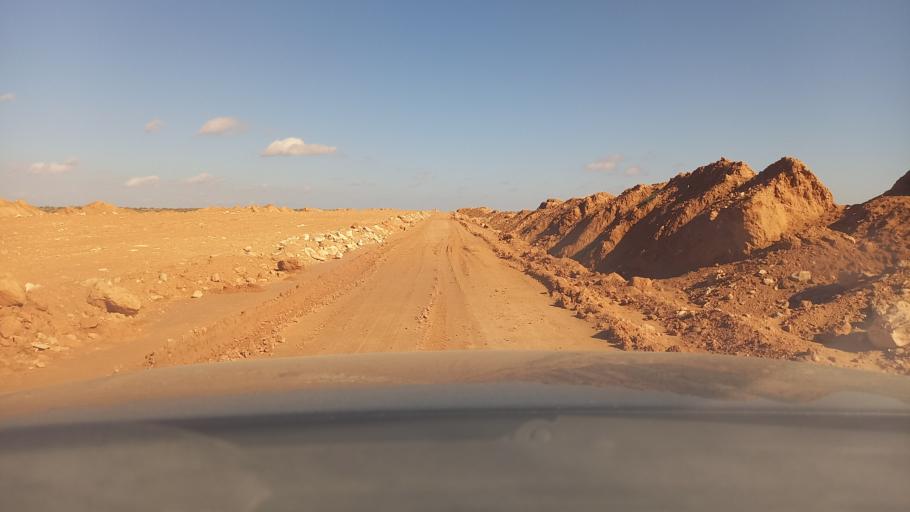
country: TN
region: Madanin
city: Medenine
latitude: 33.2423
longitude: 10.5575
